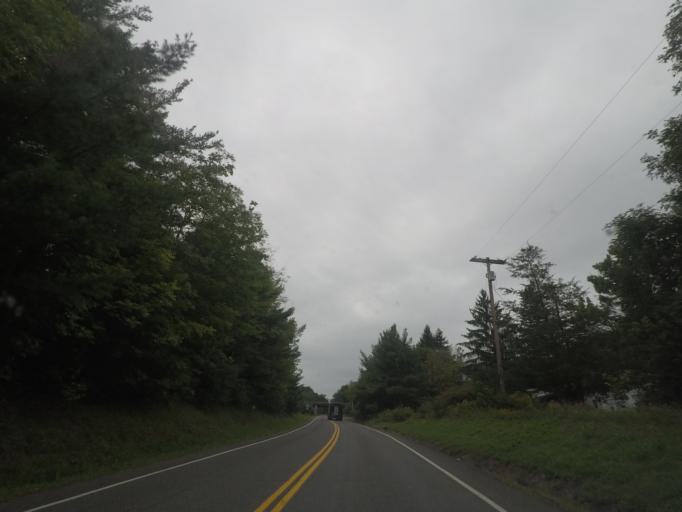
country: US
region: New York
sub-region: Columbia County
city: Chatham
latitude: 42.4061
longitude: -73.5460
